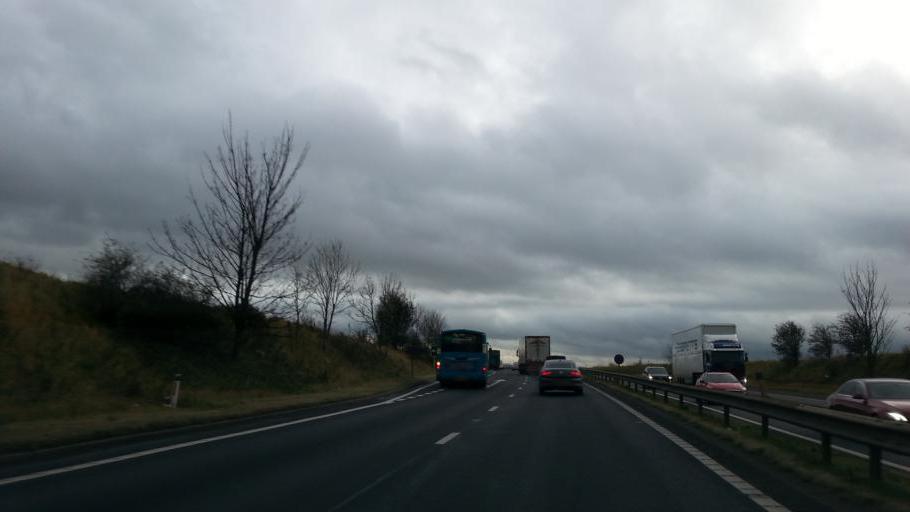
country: GB
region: England
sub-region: City and Borough of Wakefield
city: Darrington
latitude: 53.6463
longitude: -1.2557
